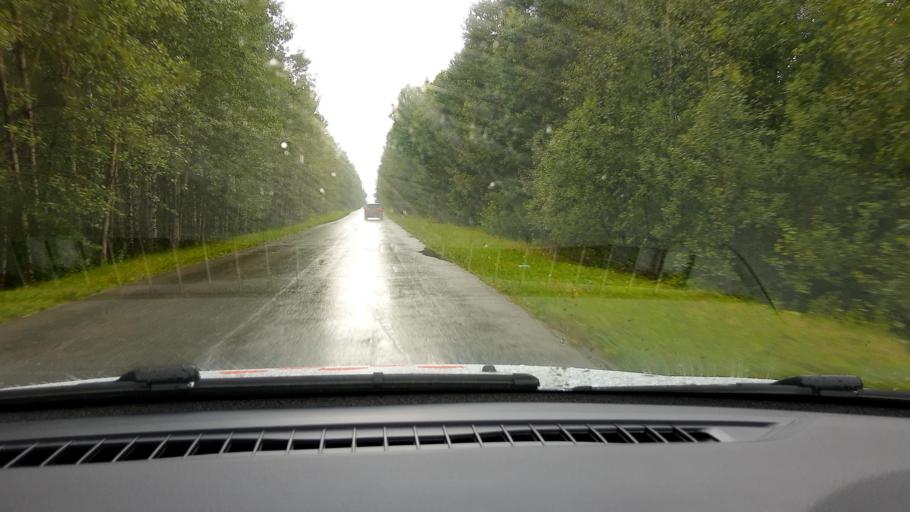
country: RU
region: Nizjnij Novgorod
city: Surovatikha
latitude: 55.9492
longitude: 43.9333
